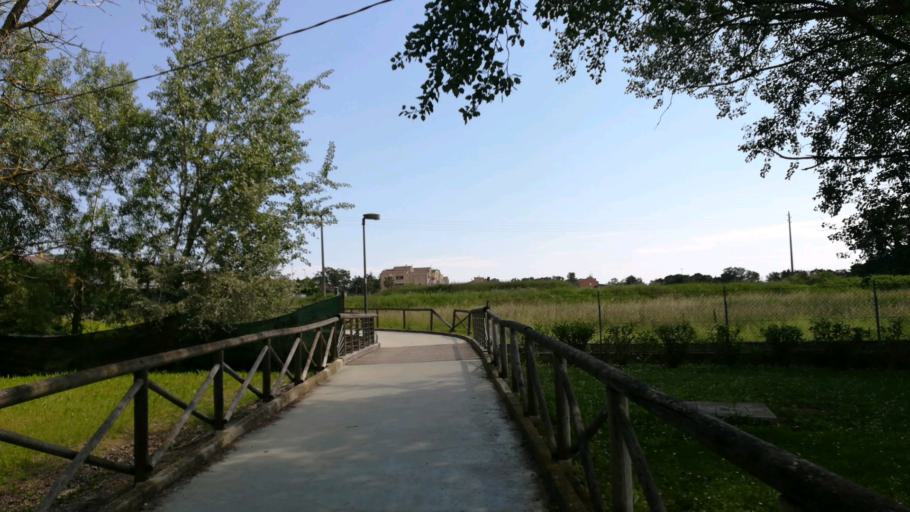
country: IT
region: The Marches
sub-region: Provincia di Macerata
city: Borgo Stazione
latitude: 43.2811
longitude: 13.6413
